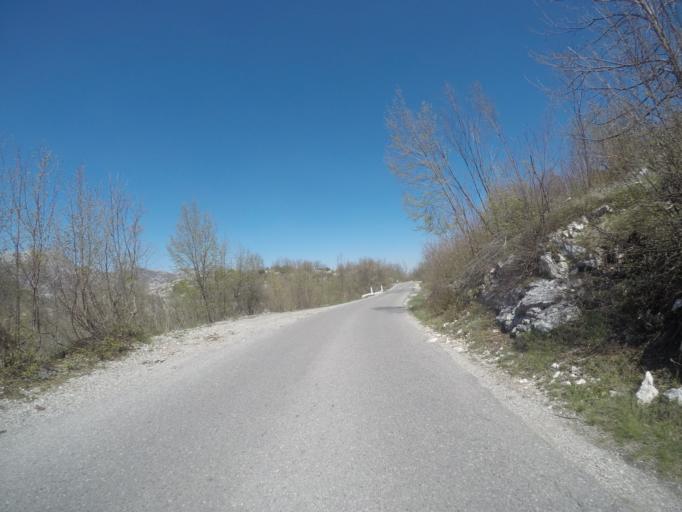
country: ME
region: Cetinje
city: Cetinje
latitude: 42.4454
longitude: 18.8735
